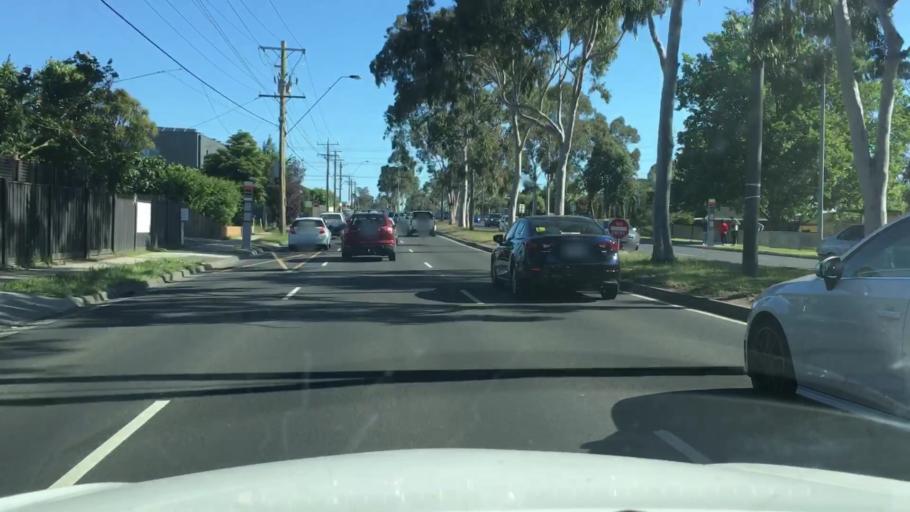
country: AU
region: Victoria
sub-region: Monash
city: Notting Hill
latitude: -37.8927
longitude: 145.1636
